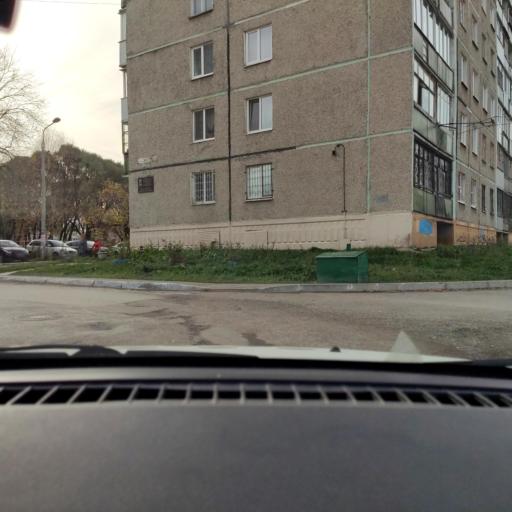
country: RU
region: Perm
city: Perm
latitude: 58.0640
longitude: 56.3476
